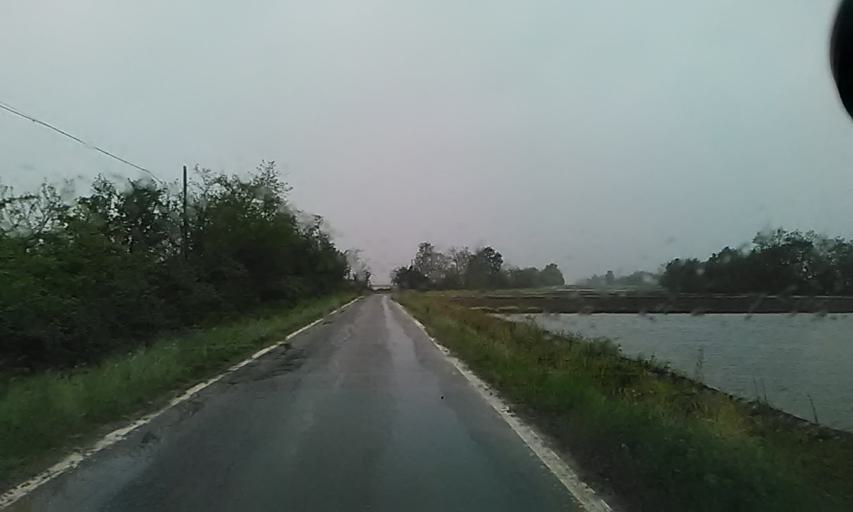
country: IT
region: Piedmont
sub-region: Provincia di Vercelli
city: San Giacomo Vercellese
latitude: 45.4904
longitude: 8.3369
